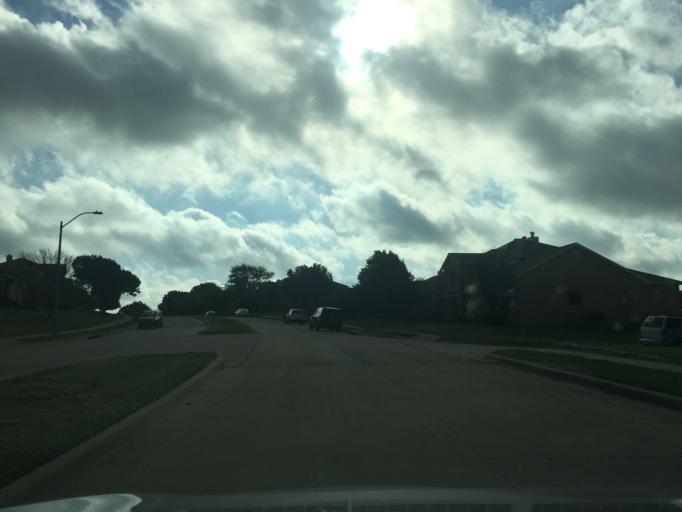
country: US
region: Texas
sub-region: Dallas County
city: Sachse
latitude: 32.9580
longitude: -96.5872
